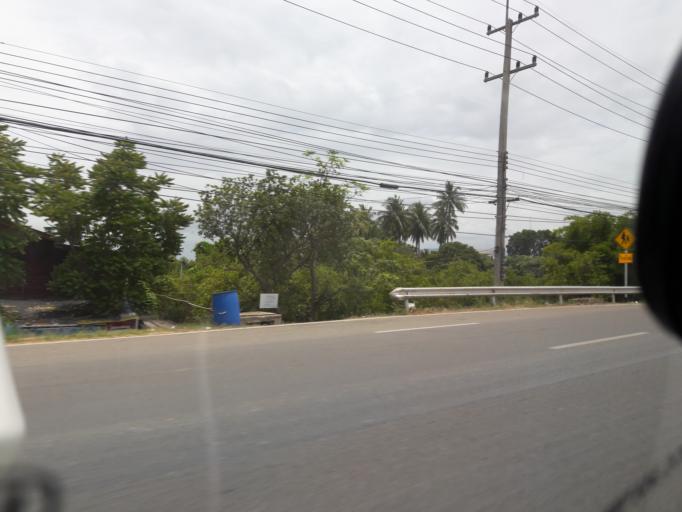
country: TH
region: Ratchaburi
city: Damnoen Saduak
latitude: 13.5532
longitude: 99.9679
